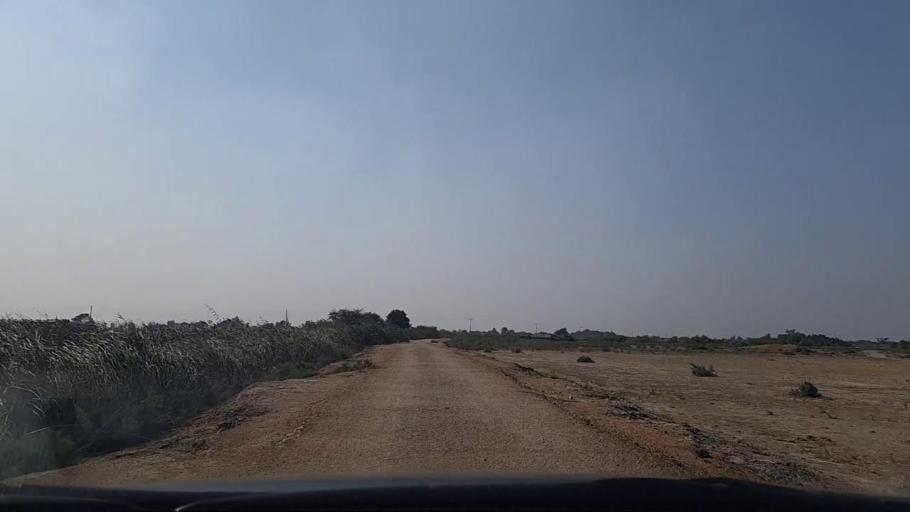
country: PK
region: Sindh
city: Mirpur Sakro
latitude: 24.5513
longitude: 67.6989
